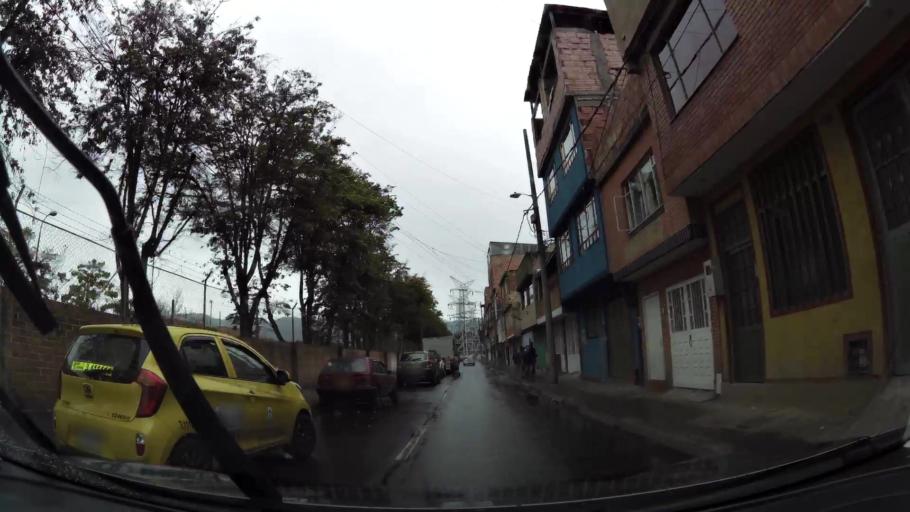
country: CO
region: Bogota D.C.
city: Bogota
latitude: 4.6602
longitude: -74.1013
